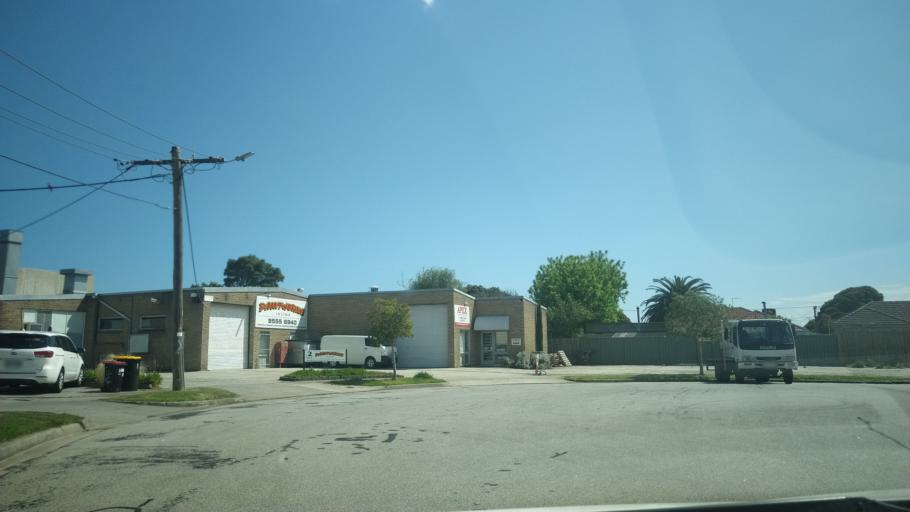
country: AU
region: Victoria
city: Highett
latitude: -37.9441
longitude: 145.0530
